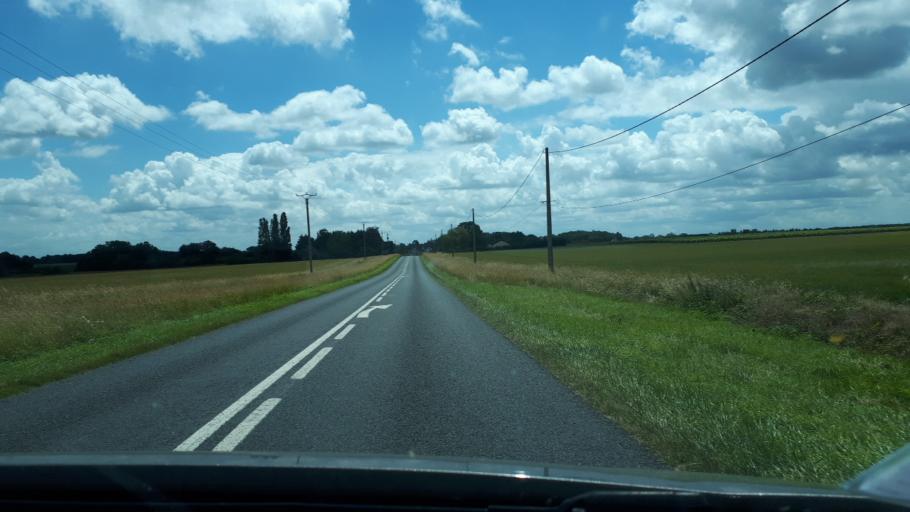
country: FR
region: Centre
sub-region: Departement du Loir-et-Cher
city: Contres
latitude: 47.3770
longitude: 1.4064
